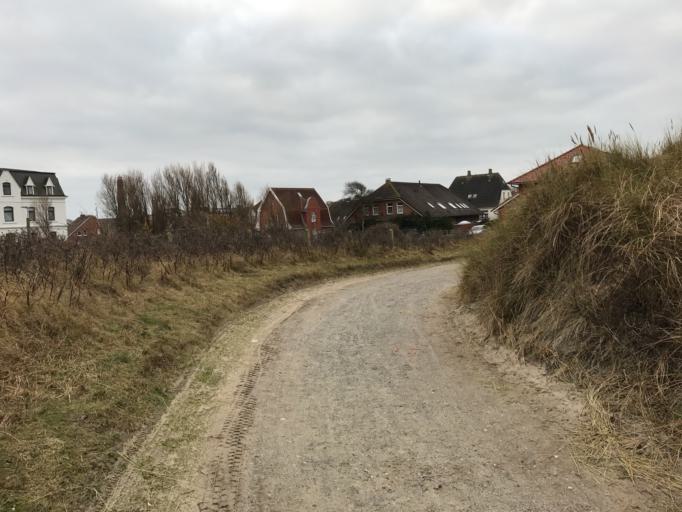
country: DE
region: Lower Saxony
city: Borkum
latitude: 53.5940
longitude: 6.6665
